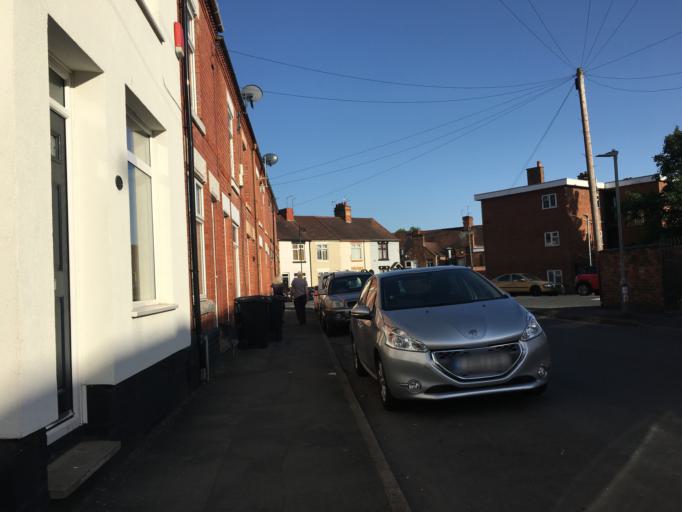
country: GB
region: England
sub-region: Warwickshire
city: Nuneaton
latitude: 52.5230
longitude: -1.4770
